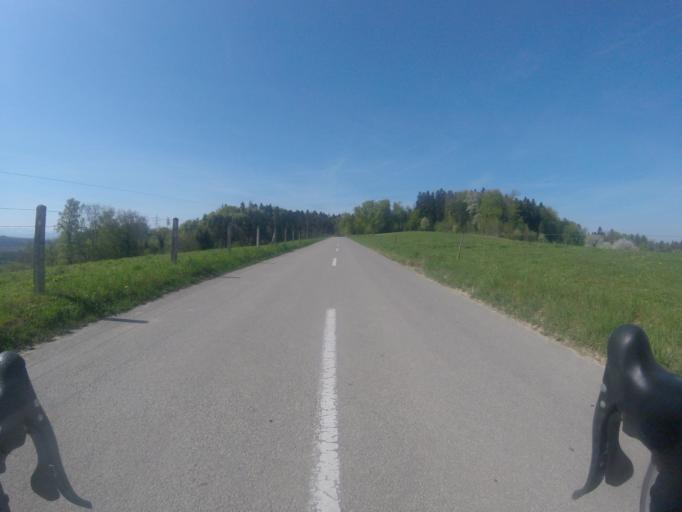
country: CH
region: Bern
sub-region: Bern-Mittelland District
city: Ferenbalm
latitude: 46.9562
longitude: 7.2354
